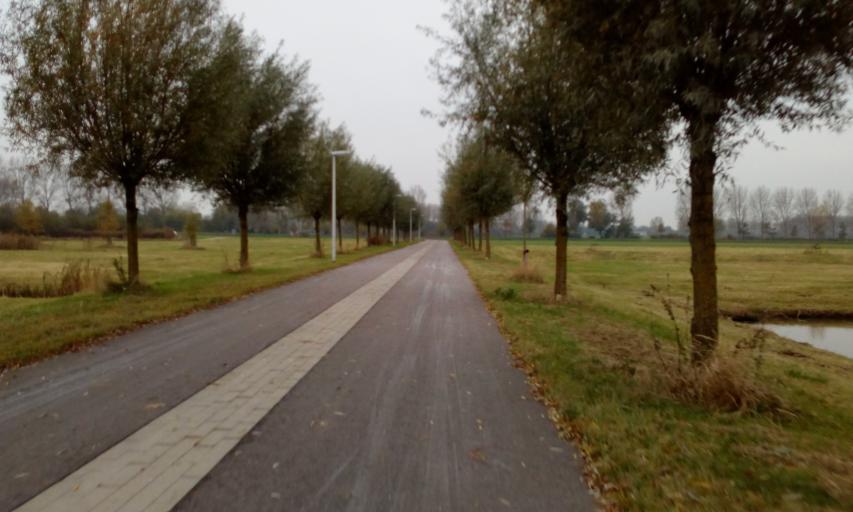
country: NL
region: South Holland
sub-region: Gemeente Lansingerland
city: Berkel en Rodenrijs
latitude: 51.9765
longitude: 4.4843
